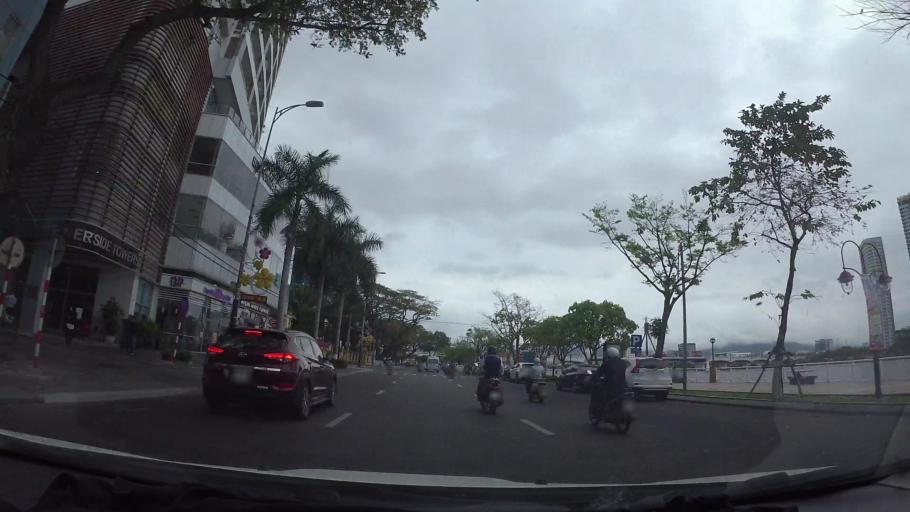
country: VN
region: Da Nang
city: Da Nang
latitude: 16.0697
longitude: 108.2250
